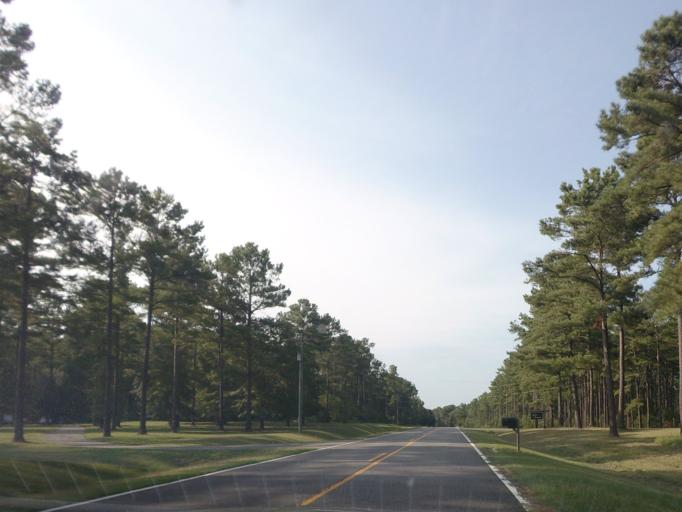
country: US
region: Georgia
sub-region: Bleckley County
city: Cochran
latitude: 32.4643
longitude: -83.2988
